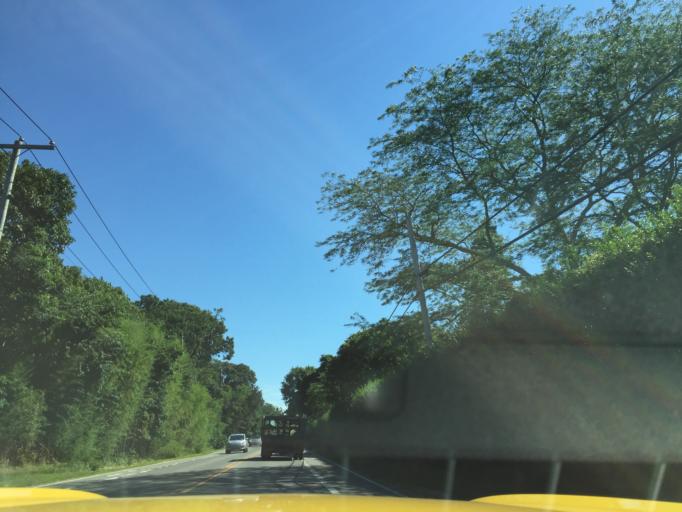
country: US
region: New York
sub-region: Suffolk County
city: Sag Harbor
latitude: 41.0158
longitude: -72.3117
